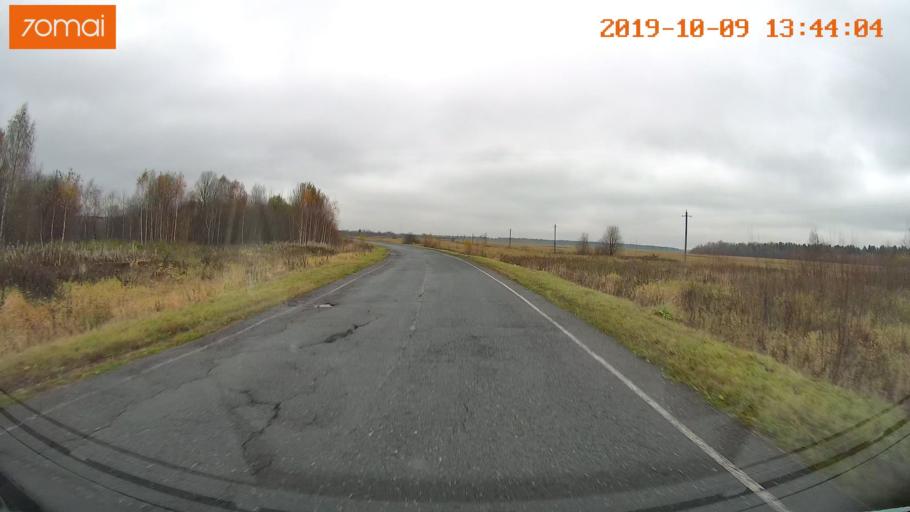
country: RU
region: Kostroma
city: Buy
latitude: 58.3633
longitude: 41.2065
